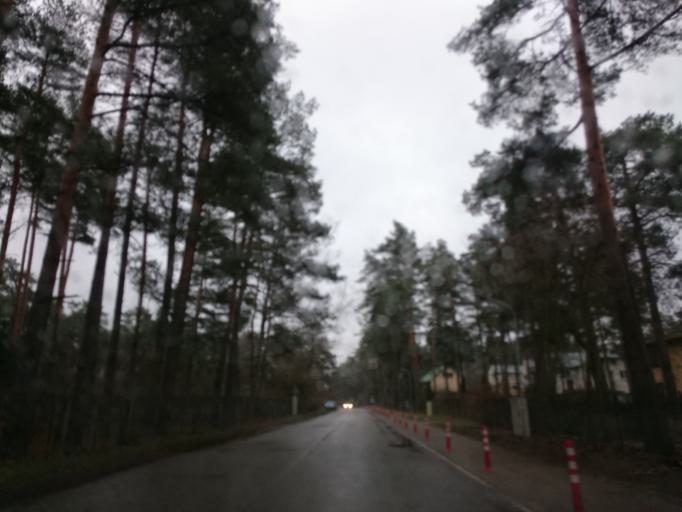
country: LV
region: Riga
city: Bergi
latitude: 57.0096
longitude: 24.3268
